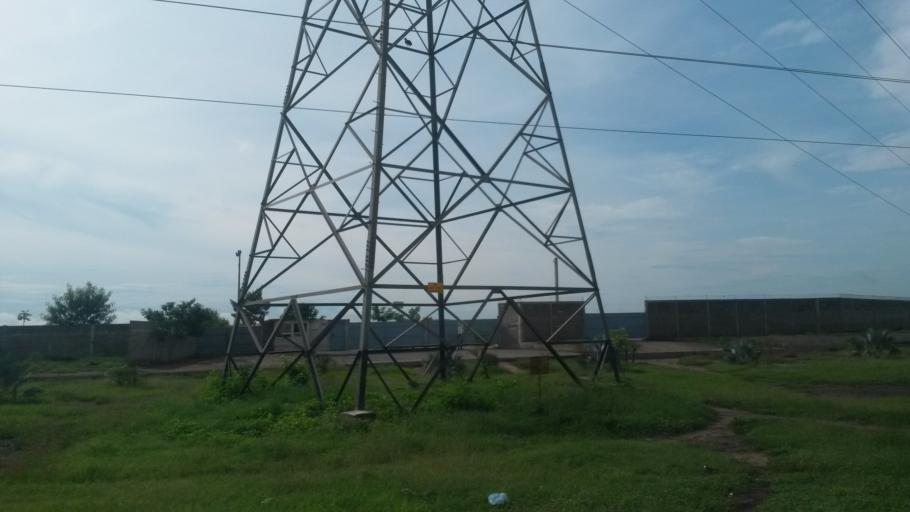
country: CO
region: Bolivar
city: Cartagena
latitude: 10.4065
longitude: -75.4521
